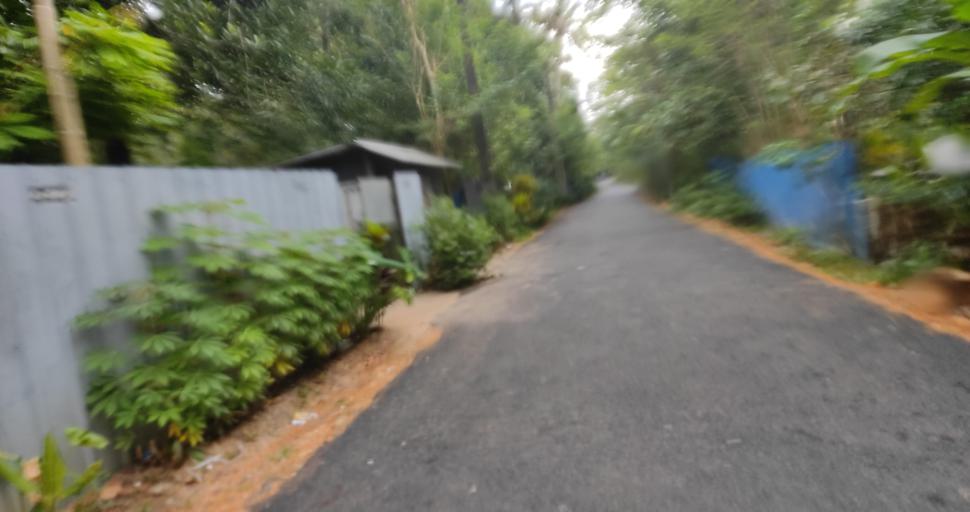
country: IN
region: Kerala
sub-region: Alappuzha
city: Shertallai
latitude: 9.6659
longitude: 76.3325
